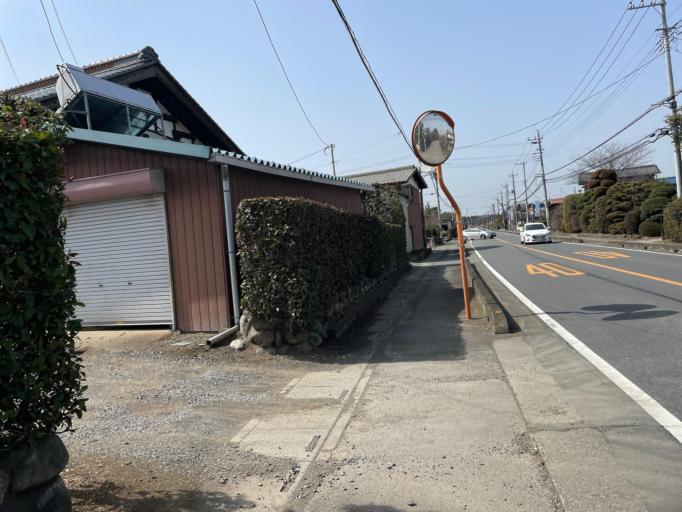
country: JP
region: Saitama
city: Ogawa
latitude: 36.1025
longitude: 139.2693
